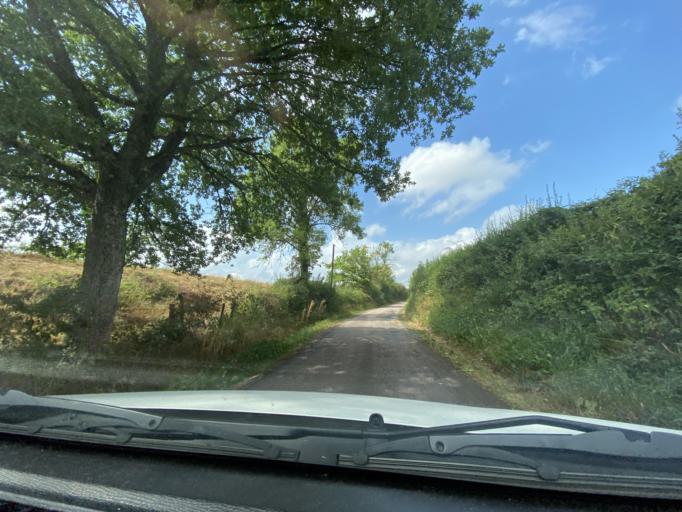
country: FR
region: Bourgogne
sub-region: Departement de la Cote-d'Or
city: Saulieu
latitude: 47.2852
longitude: 4.2380
